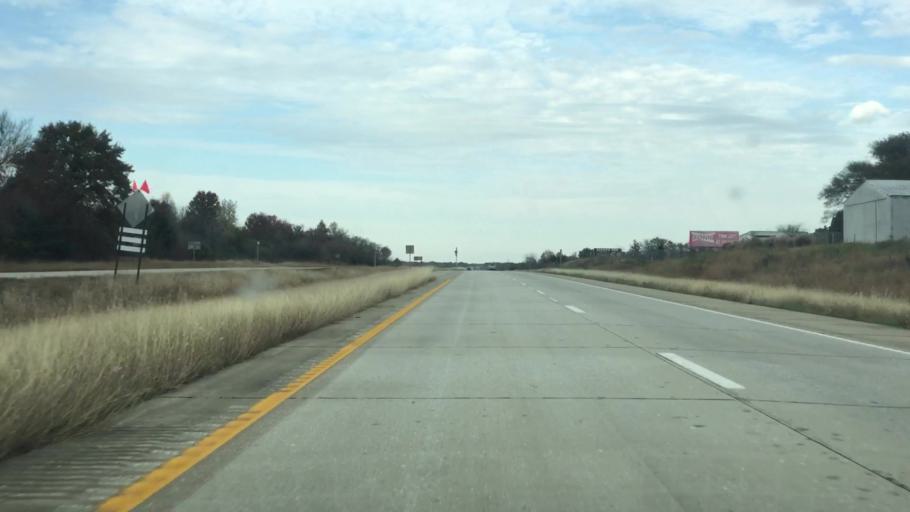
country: US
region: Missouri
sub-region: Henry County
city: Clinton
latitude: 38.3069
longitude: -93.7583
